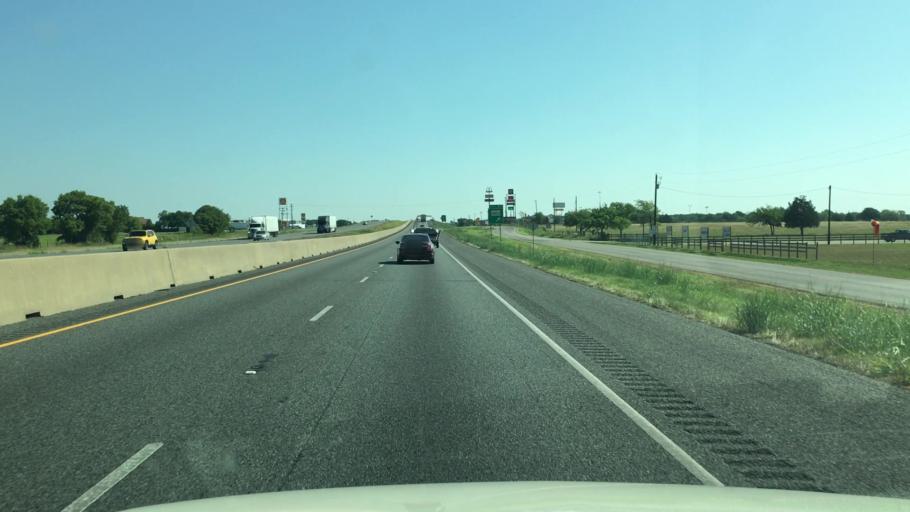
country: US
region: Texas
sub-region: Hunt County
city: Caddo Mills
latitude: 33.0384
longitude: -96.1835
